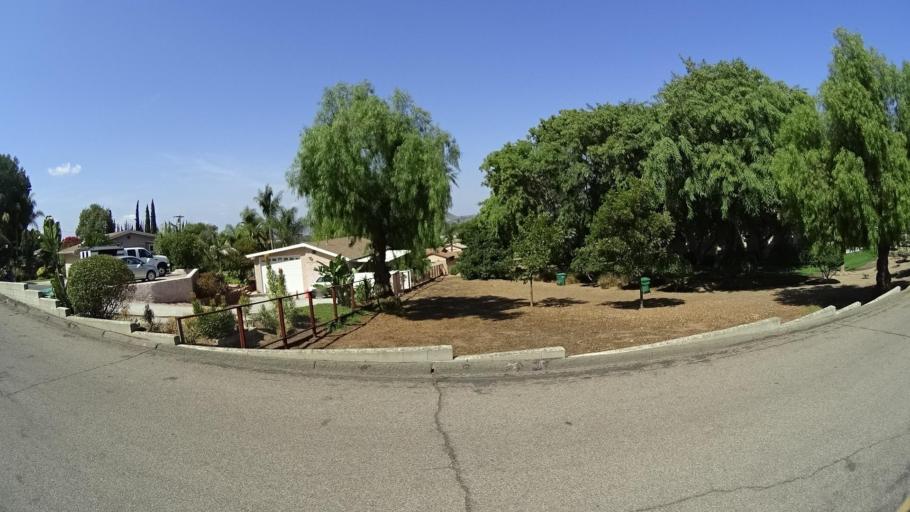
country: US
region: California
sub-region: San Diego County
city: Granite Hills
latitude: 32.7786
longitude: -116.9195
